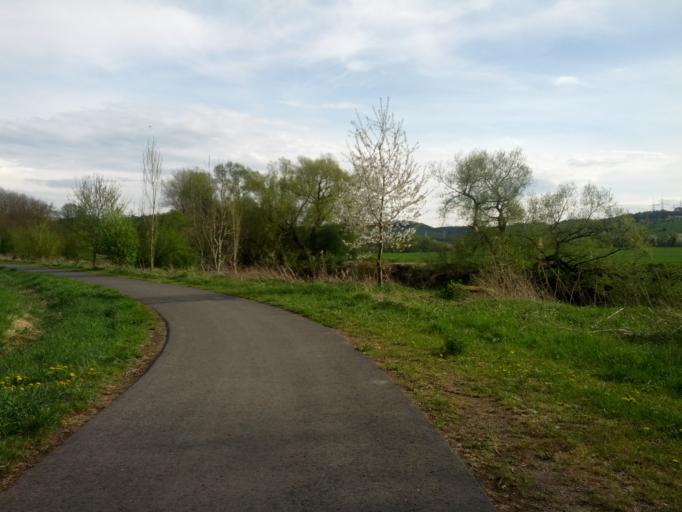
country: DE
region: Thuringia
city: Creuzburg
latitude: 51.0300
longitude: 10.2328
